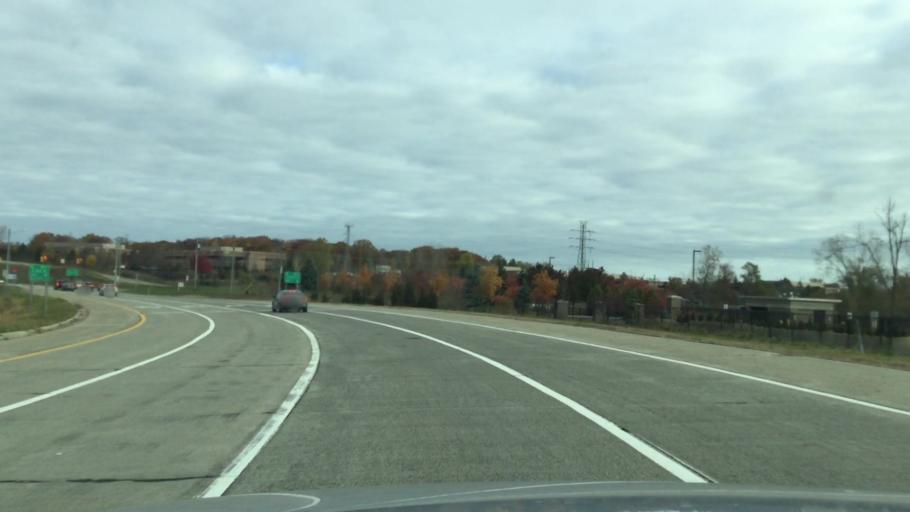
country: US
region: Michigan
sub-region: Oakland County
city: Novi
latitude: 42.4946
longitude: -83.4442
